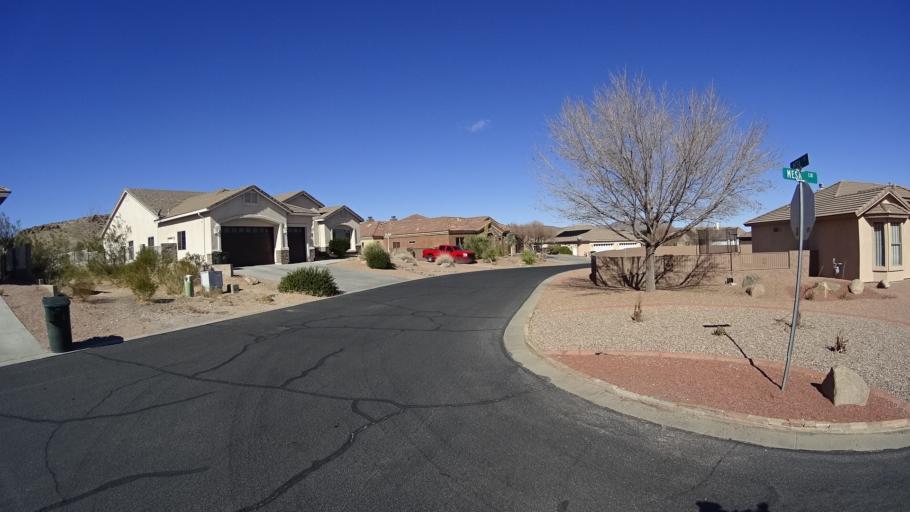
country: US
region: Arizona
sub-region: Mohave County
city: Kingman
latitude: 35.1880
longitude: -114.0263
